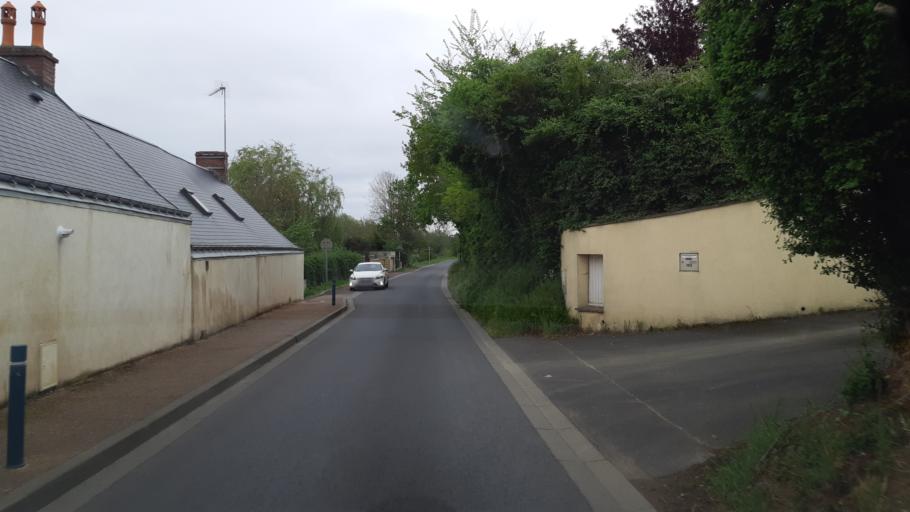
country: FR
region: Lower Normandy
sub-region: Departement de la Manche
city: Donville-les-Bains
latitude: 48.8522
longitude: -1.5535
